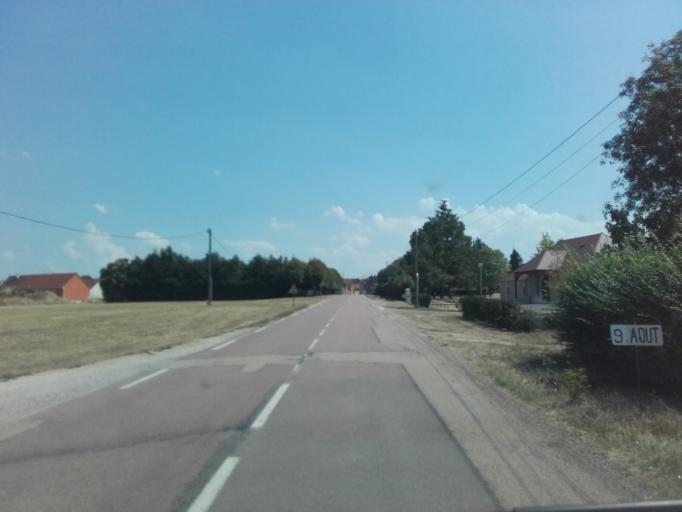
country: FR
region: Bourgogne
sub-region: Departement de l'Yonne
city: Joux-la-Ville
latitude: 47.6760
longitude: 3.8747
